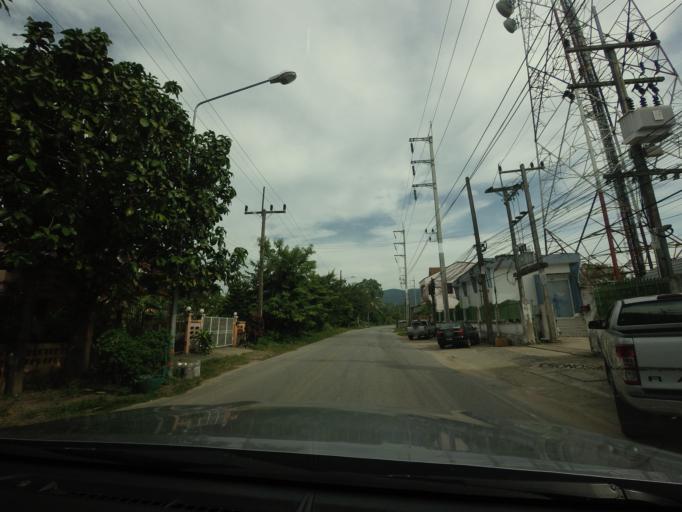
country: TH
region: Yala
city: Yala
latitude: 6.5219
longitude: 101.2890
